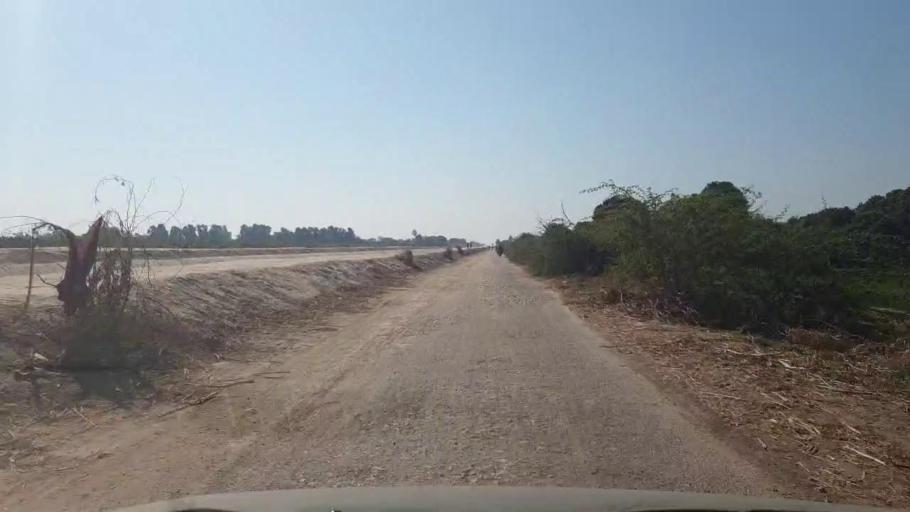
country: PK
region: Sindh
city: Mirwah Gorchani
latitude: 25.3026
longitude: 69.1029
